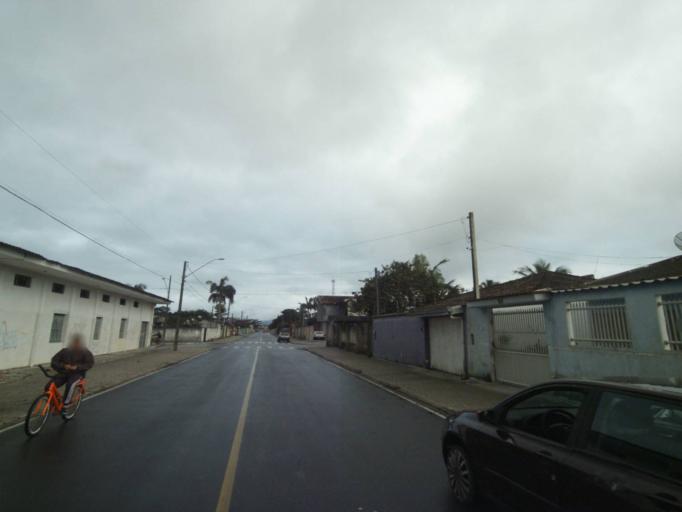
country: BR
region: Parana
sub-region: Paranagua
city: Paranagua
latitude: -25.5705
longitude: -48.5716
